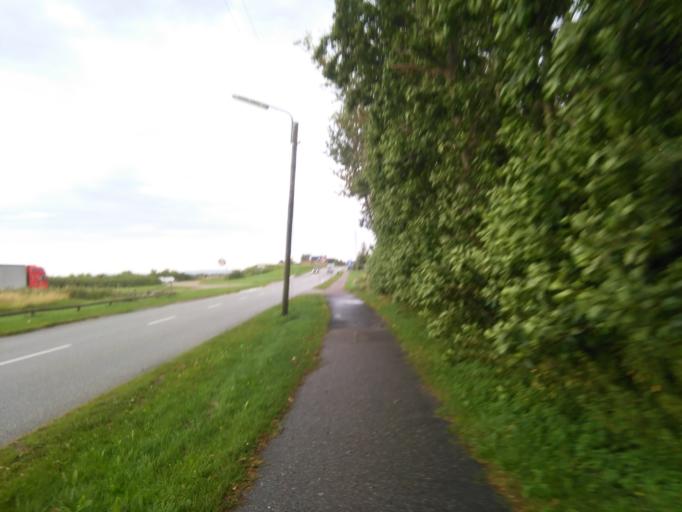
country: DK
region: Central Jutland
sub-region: Arhus Kommune
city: Hjortshoj
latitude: 56.2237
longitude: 10.3013
